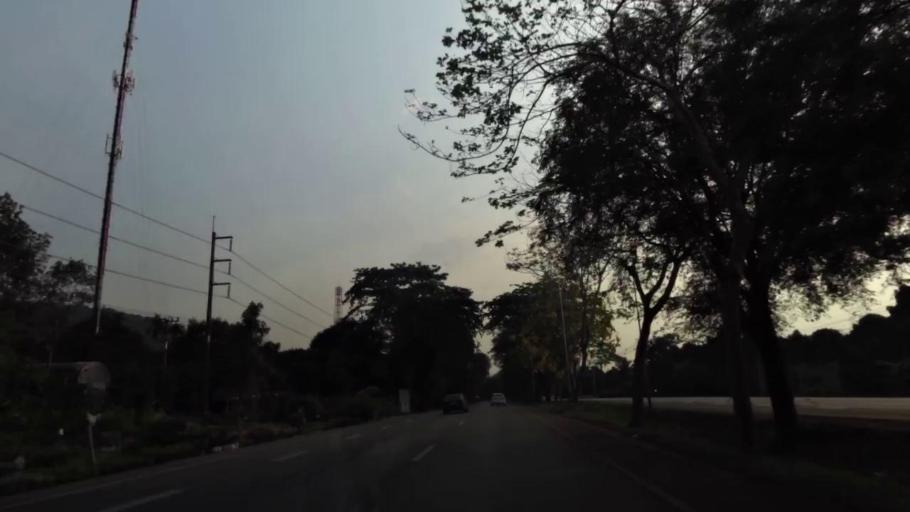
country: TH
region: Chanthaburi
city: Chanthaburi
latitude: 12.5662
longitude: 102.1615
